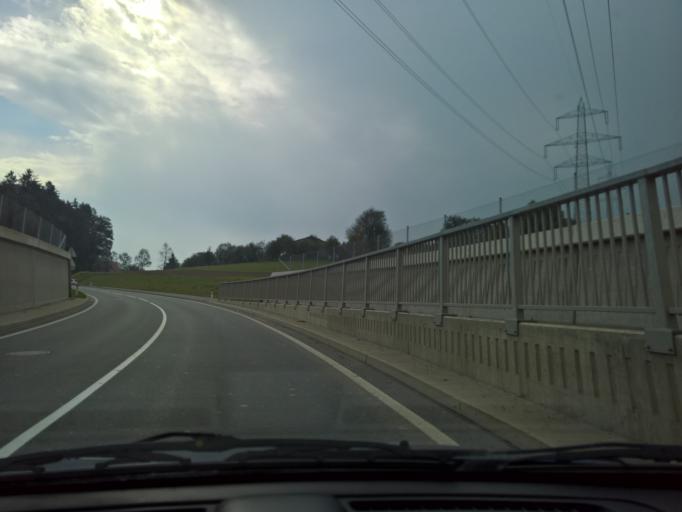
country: AT
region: Styria
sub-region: Politischer Bezirk Deutschlandsberg
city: Gross Sankt Florian
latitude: 46.8129
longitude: 15.3153
